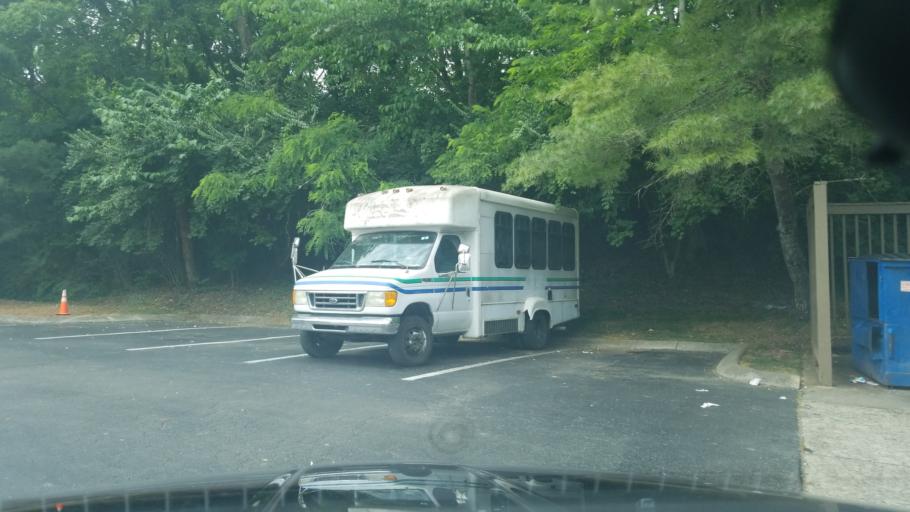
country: US
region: Tennessee
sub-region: Davidson County
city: Goodlettsville
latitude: 36.2691
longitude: -86.7427
